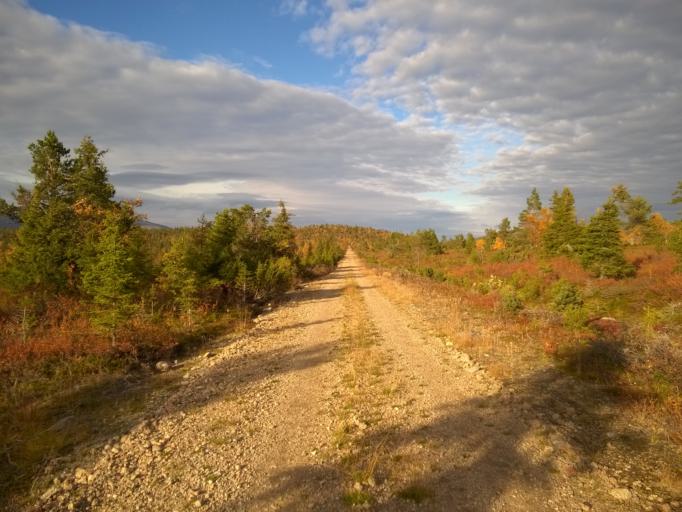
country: FI
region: Lapland
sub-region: Tunturi-Lappi
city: Muonio
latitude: 67.9792
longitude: 24.1052
